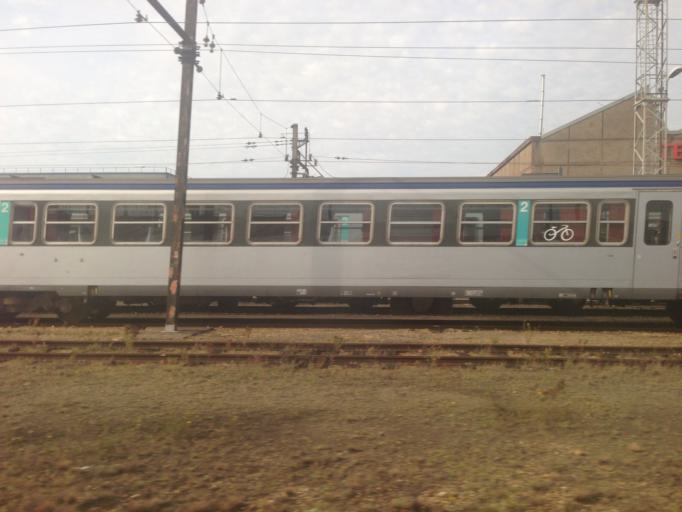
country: FR
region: Centre
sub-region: Departement d'Indre-et-Loire
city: Saint-Pierre-des-Corps
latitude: 47.3882
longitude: 0.7378
